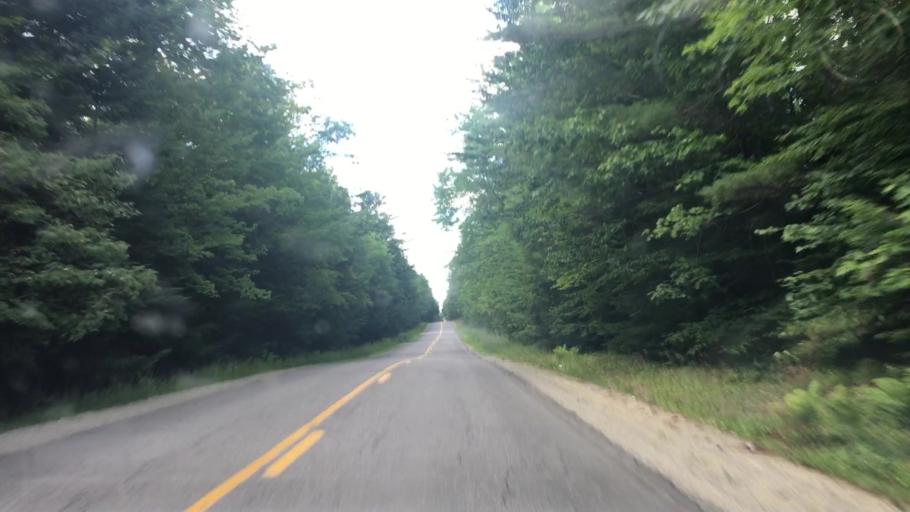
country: US
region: Maine
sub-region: Franklin County
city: Chesterville
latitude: 44.5932
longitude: -70.0860
